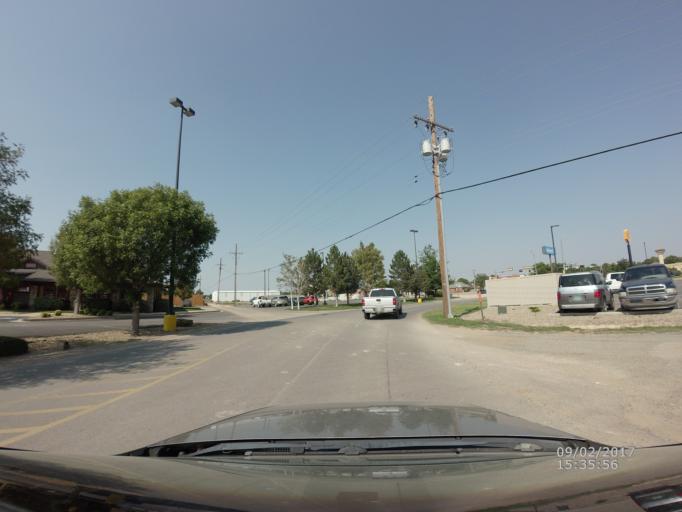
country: US
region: New Mexico
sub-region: Curry County
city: Clovis
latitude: 34.4390
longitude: -103.1973
